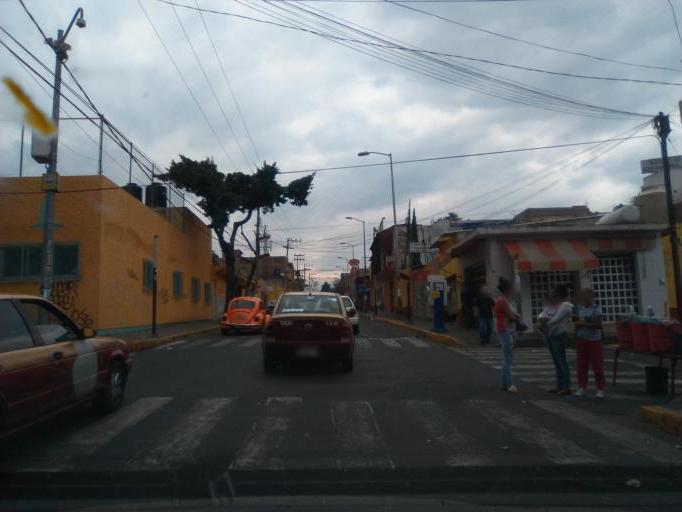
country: MX
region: Mexico City
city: Alvaro Obregon
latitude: 19.3712
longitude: -99.2196
